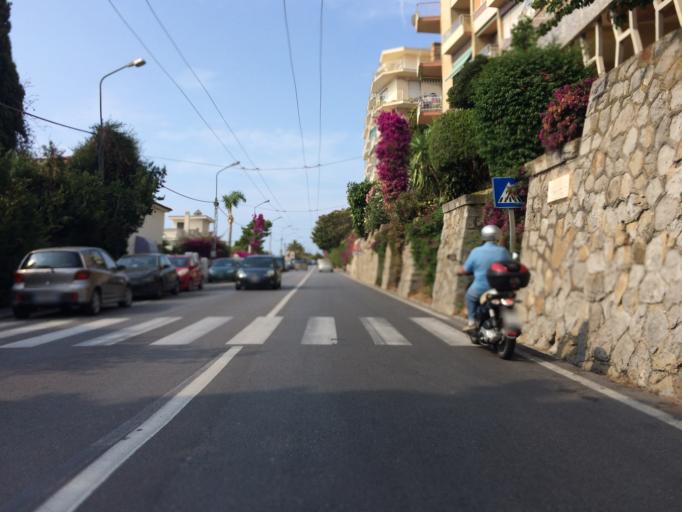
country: IT
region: Liguria
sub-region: Provincia di Imperia
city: Ospedaletti
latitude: 43.7999
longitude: 7.7417
